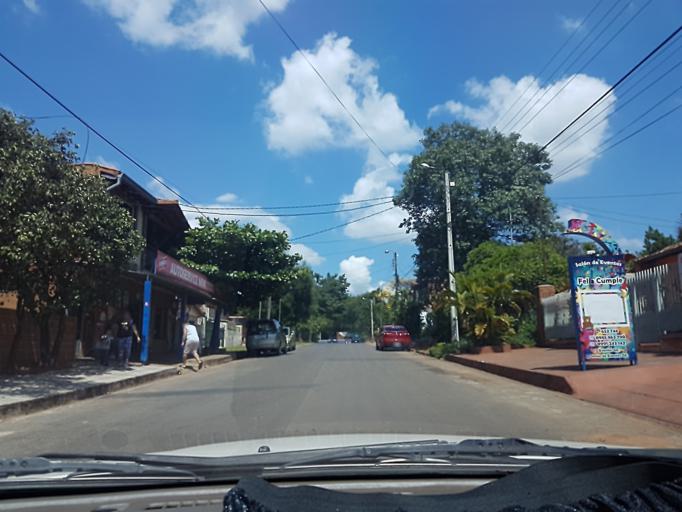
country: PY
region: Central
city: San Lorenzo
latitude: -25.2622
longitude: -57.4978
